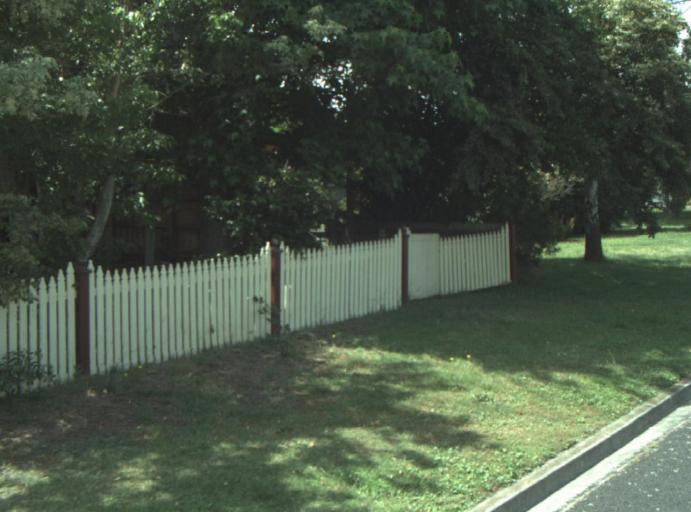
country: AU
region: Victoria
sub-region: Greater Geelong
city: Clifton Springs
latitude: -38.1598
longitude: 144.5680
